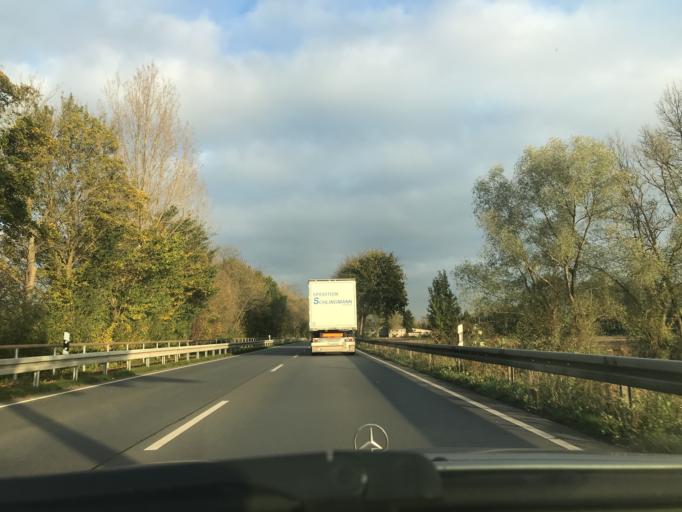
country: DE
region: North Rhine-Westphalia
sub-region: Regierungsbezirk Arnsberg
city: Soest
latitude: 51.6219
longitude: 8.1021
